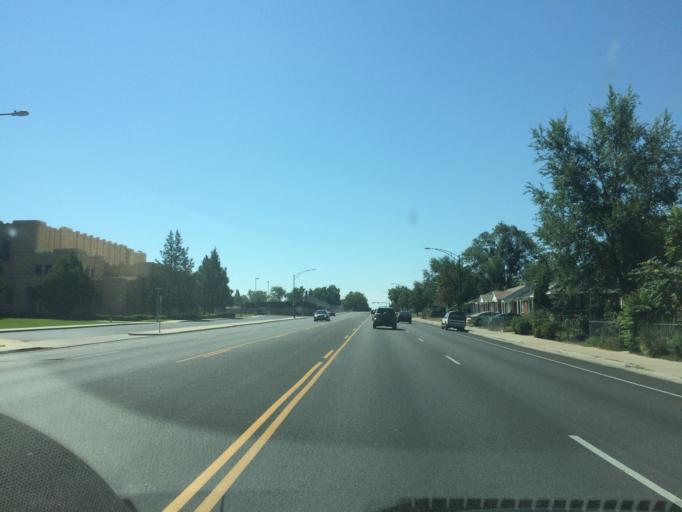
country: US
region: Utah
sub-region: Weber County
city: Ogden
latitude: 41.2135
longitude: -111.9484
